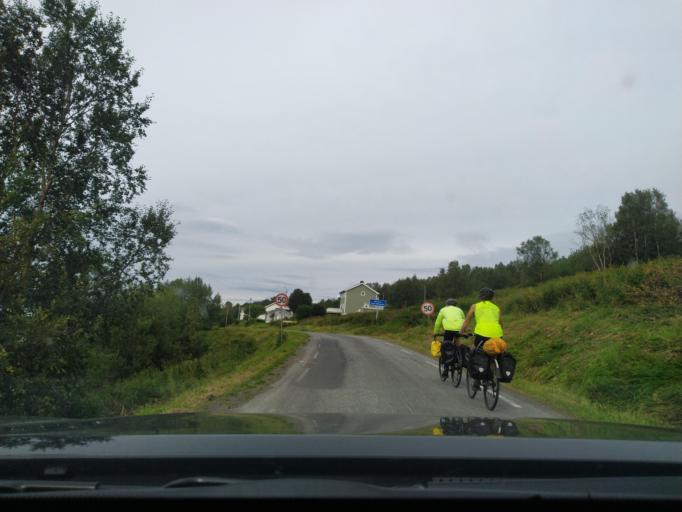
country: NO
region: Nordland
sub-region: Evenes
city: Randa
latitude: 68.7274
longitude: 16.8582
